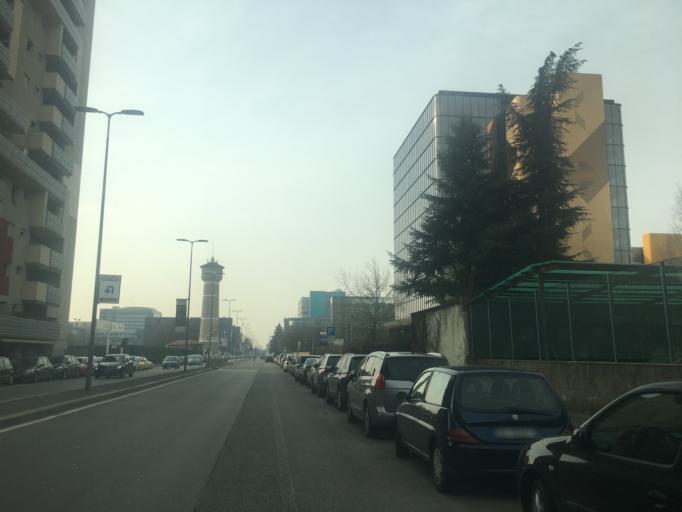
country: IT
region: Lombardy
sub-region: Citta metropolitana di Milano
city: Sesto San Giovanni
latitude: 45.5244
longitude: 9.2135
